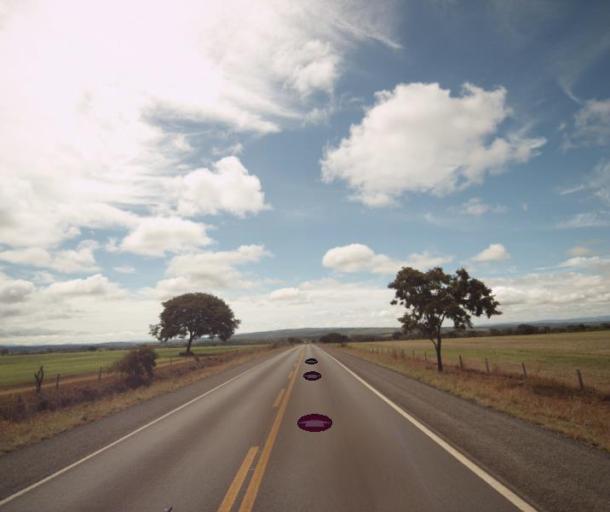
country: BR
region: Goias
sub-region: Padre Bernardo
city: Padre Bernardo
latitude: -15.2167
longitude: -48.6081
